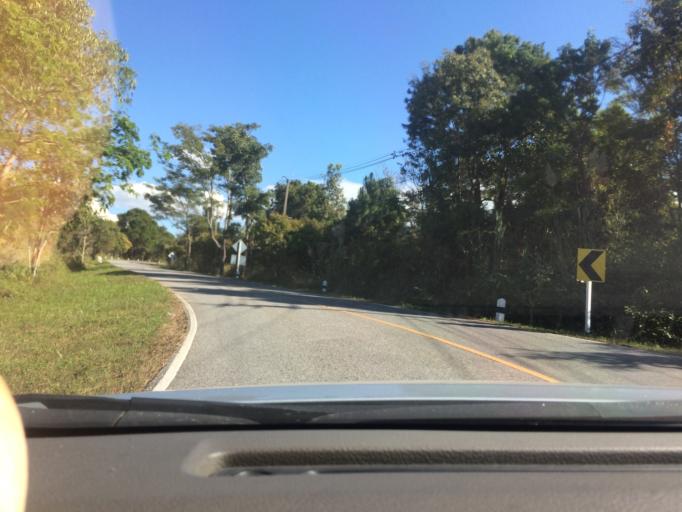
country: TH
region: Phitsanulok
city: Nakhon Thai
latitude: 17.0190
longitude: 100.9854
